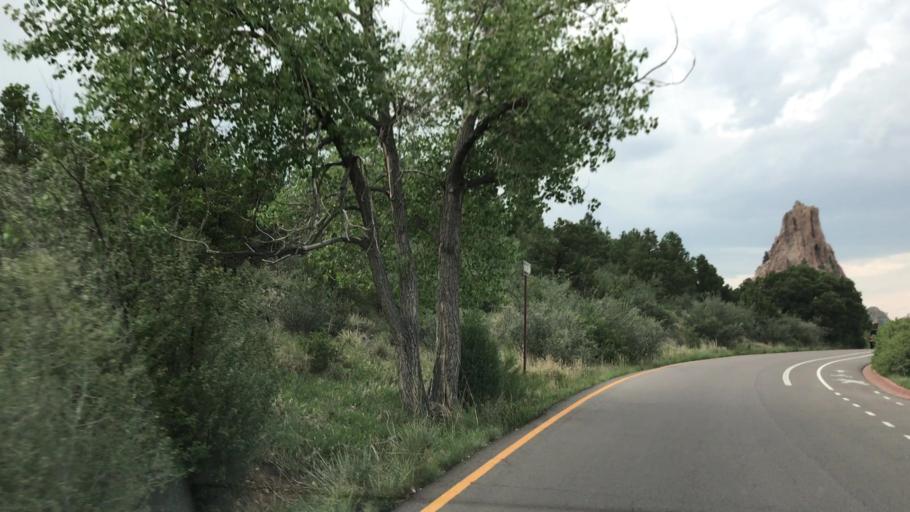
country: US
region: Colorado
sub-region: El Paso County
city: Manitou Springs
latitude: 38.8690
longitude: -104.8786
